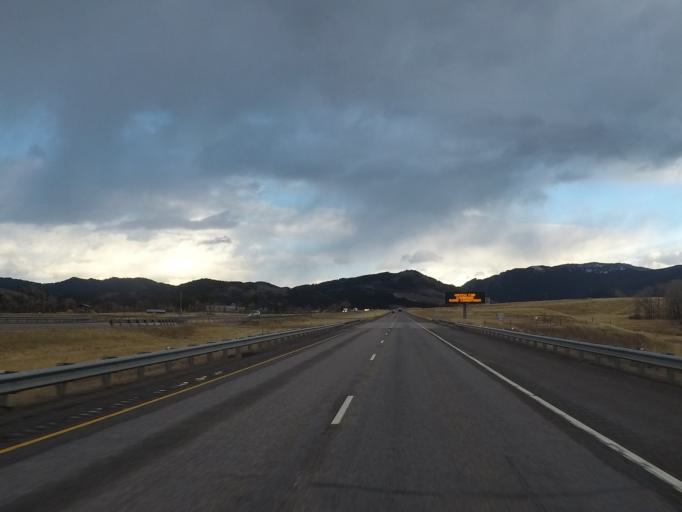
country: US
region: Montana
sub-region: Gallatin County
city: Bozeman
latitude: 45.6664
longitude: -110.9815
